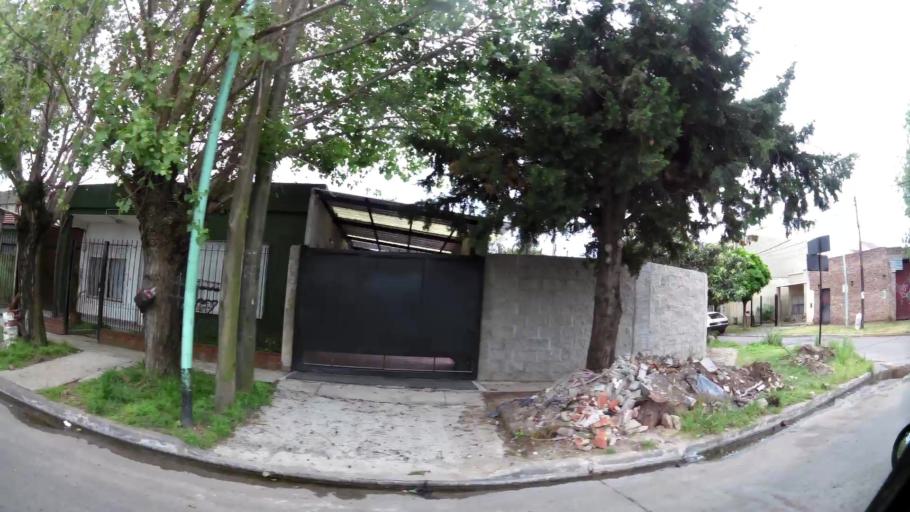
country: AR
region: Buenos Aires
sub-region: Partido de Quilmes
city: Quilmes
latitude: -34.7562
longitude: -58.2222
